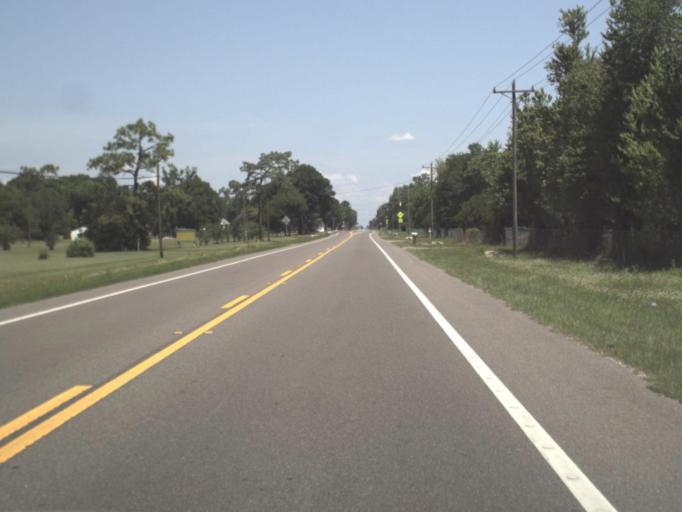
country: US
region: Florida
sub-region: Clay County
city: Keystone Heights
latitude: 29.8357
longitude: -82.0637
